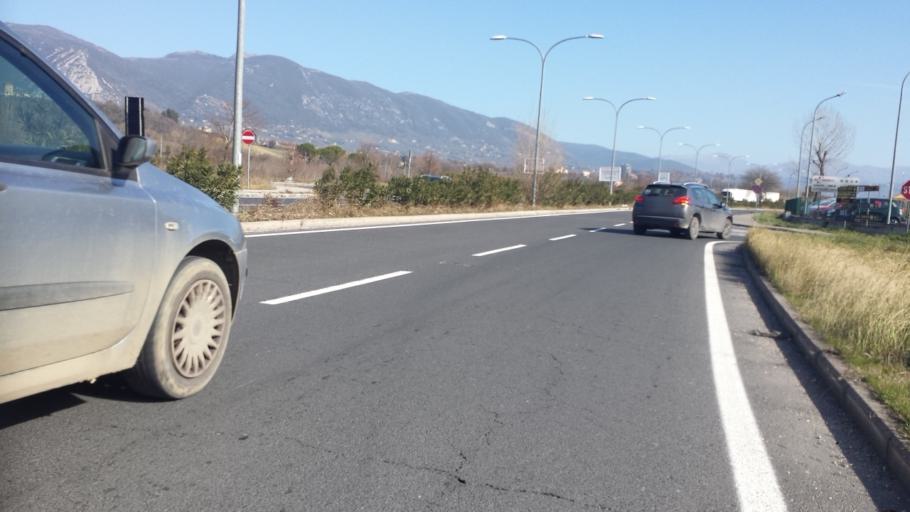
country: IT
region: Umbria
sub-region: Provincia di Terni
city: Terni
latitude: 42.5672
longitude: 12.5991
